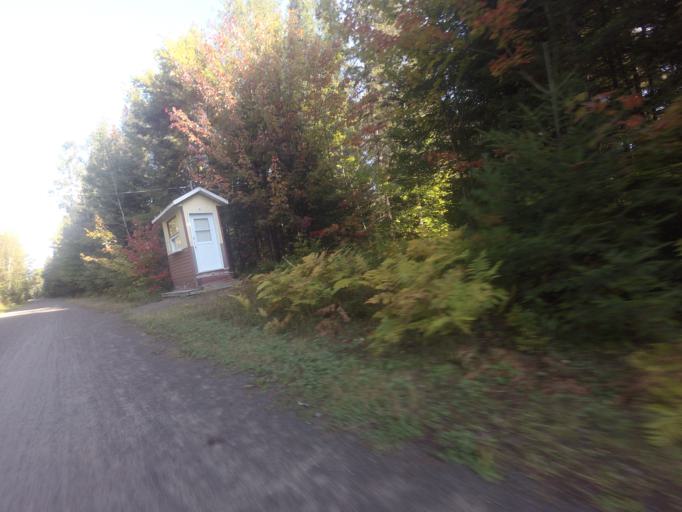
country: CA
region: Quebec
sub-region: Laurentides
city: Val-David
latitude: 46.0215
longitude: -74.1921
